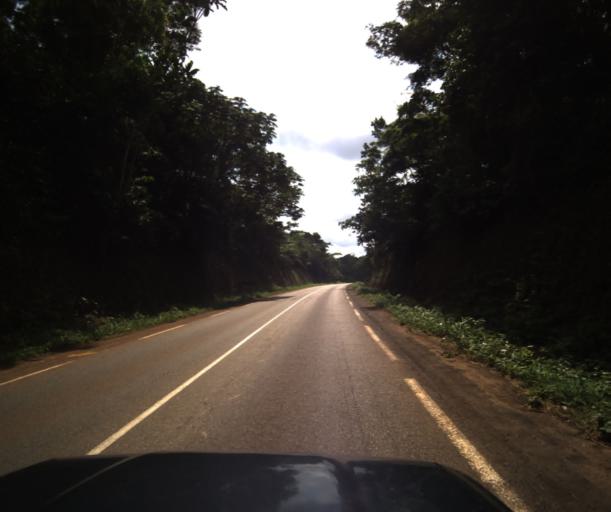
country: CM
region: Centre
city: Eseka
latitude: 3.8734
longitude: 10.6278
